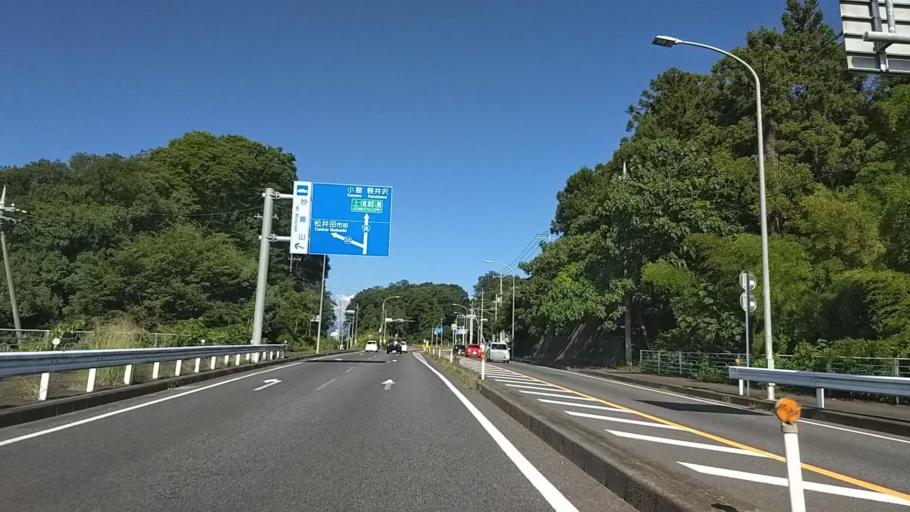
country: JP
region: Gunma
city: Annaka
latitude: 36.3084
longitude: 138.8184
